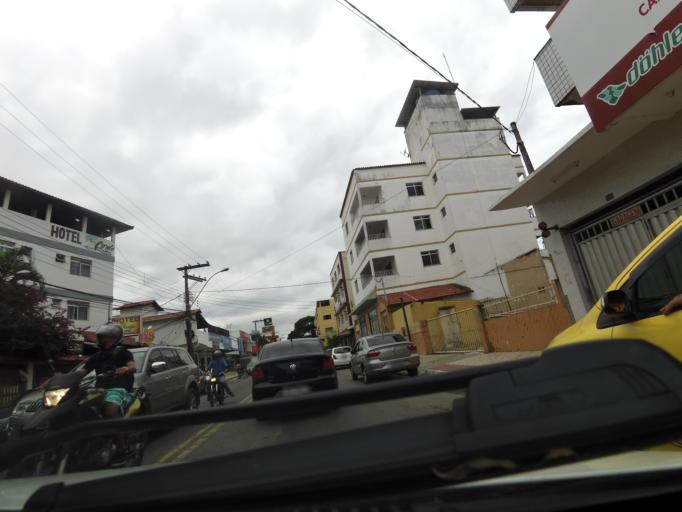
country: BR
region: Espirito Santo
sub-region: Guarapari
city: Guarapari
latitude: -20.6641
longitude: -40.4926
